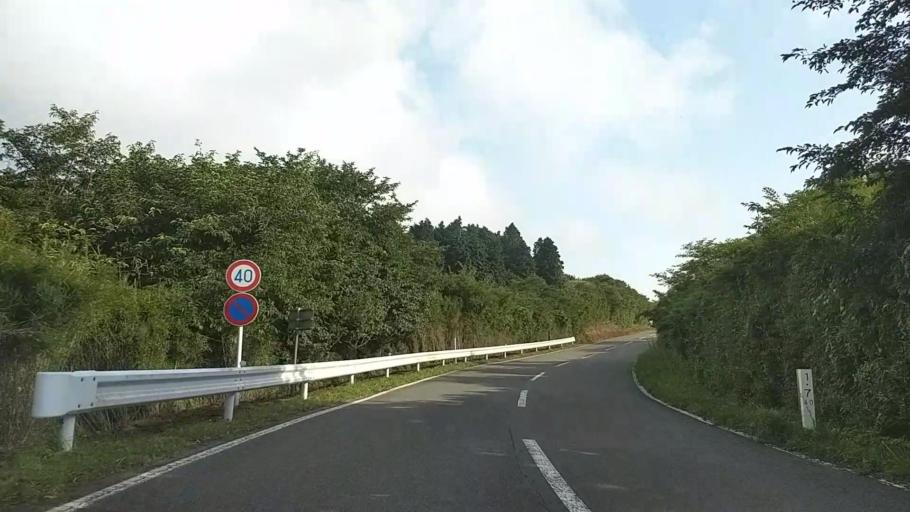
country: JP
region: Kanagawa
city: Hakone
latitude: 35.1899
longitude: 139.0020
